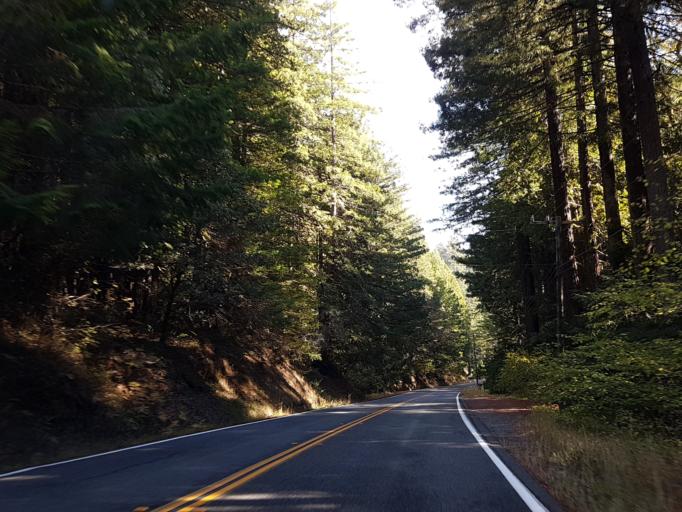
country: US
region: California
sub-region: Humboldt County
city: Rio Dell
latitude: 40.4095
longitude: -123.9551
